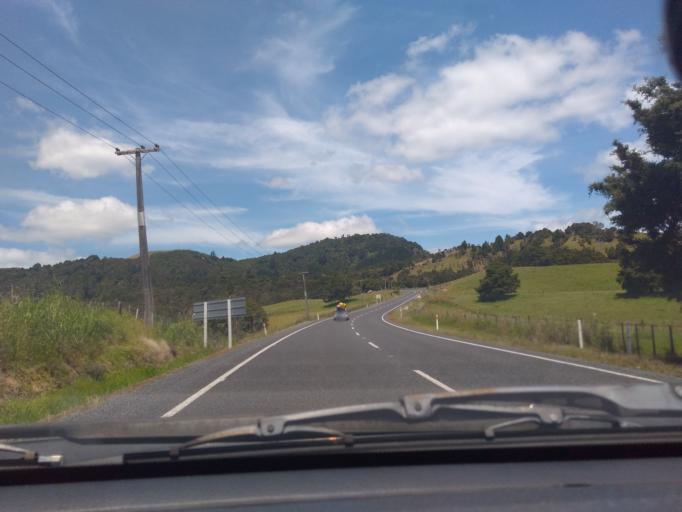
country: NZ
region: Northland
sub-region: Far North District
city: Kerikeri
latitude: -35.1147
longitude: 173.8144
